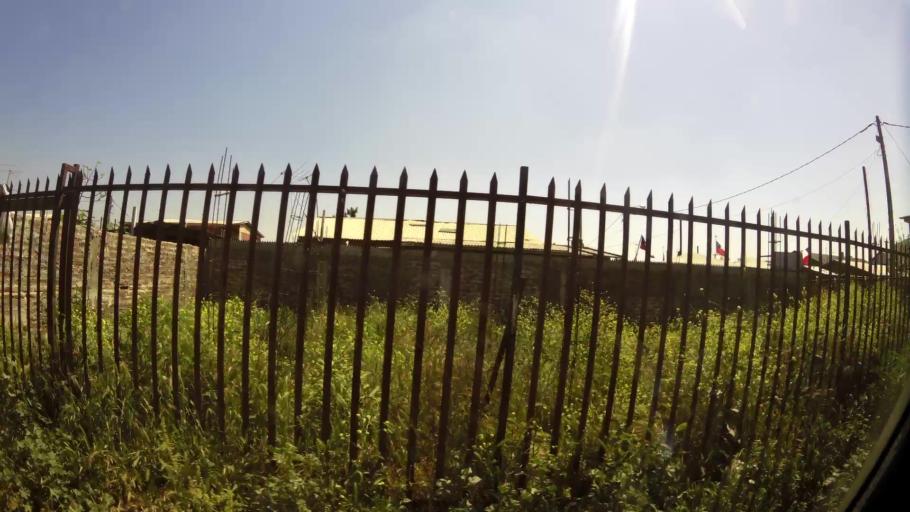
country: CL
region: Santiago Metropolitan
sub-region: Provincia de Talagante
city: Penaflor
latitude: -33.5927
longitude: -70.8128
